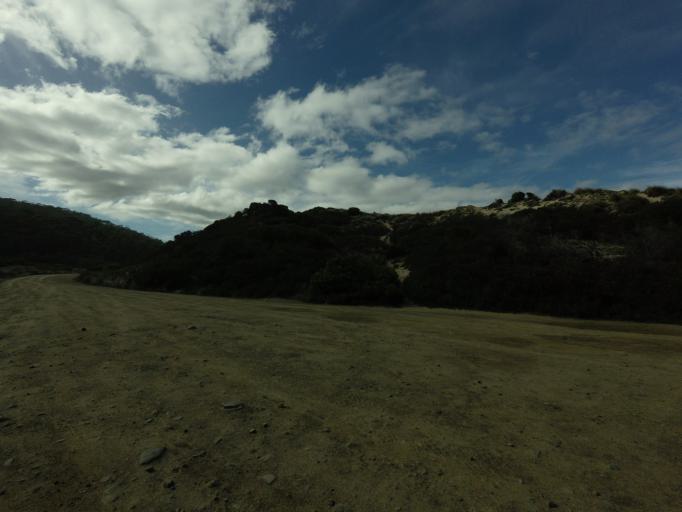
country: AU
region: Tasmania
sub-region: Clarence
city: Sandford
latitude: -43.0853
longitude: 147.6735
